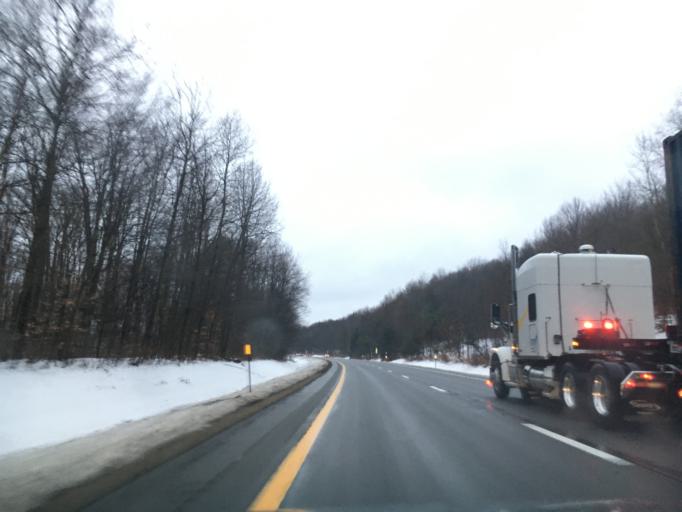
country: US
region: New York
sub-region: Cortland County
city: McGraw
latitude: 42.5180
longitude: -76.0798
